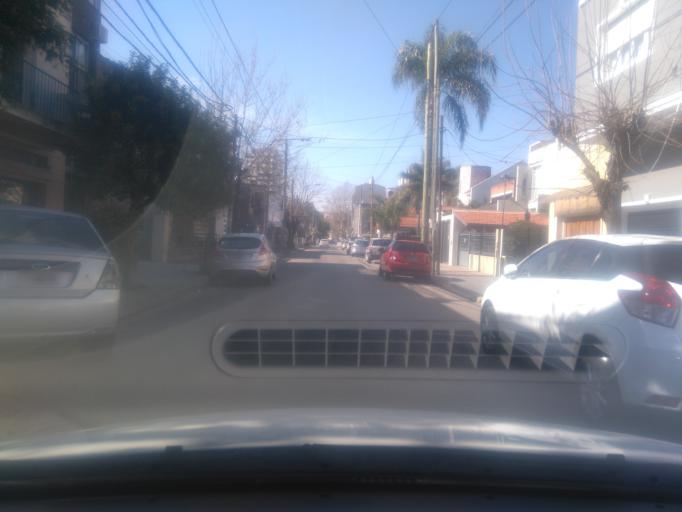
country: AR
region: Buenos Aires
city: San Justo
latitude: -34.6458
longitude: -58.5676
